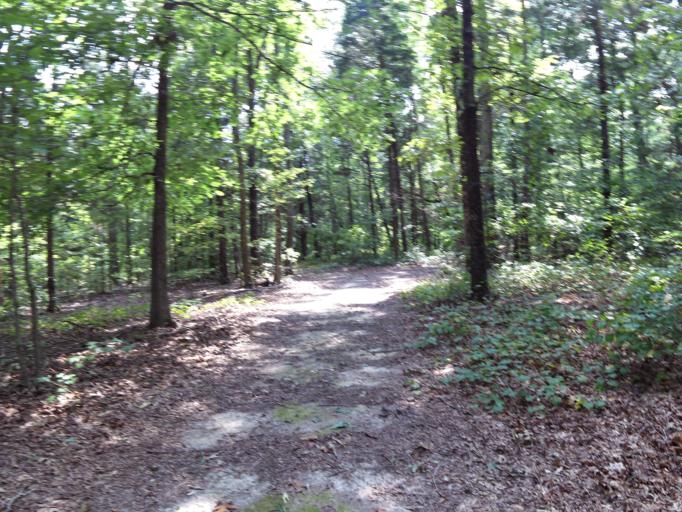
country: US
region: Tennessee
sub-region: Hardin County
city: Crump
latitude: 35.1491
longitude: -88.3238
